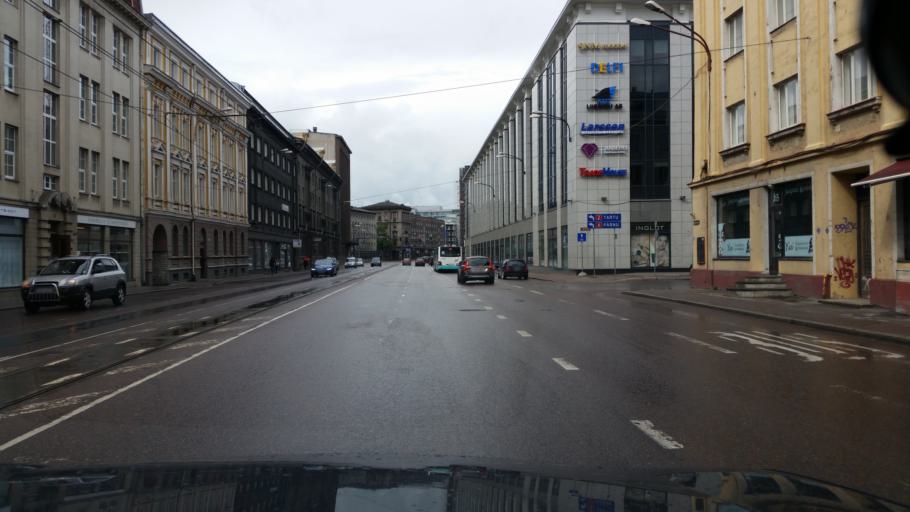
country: EE
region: Harju
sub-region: Tallinna linn
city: Tallinn
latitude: 59.4380
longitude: 24.7679
